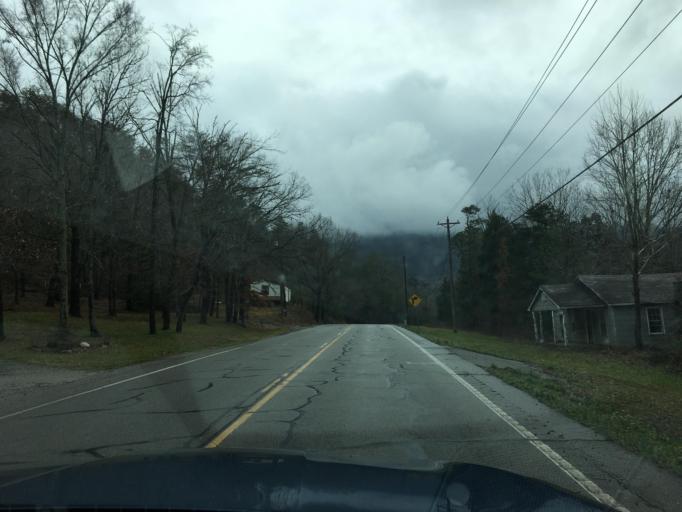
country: US
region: Tennessee
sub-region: Polk County
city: Benton
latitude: 35.1663
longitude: -84.6367
